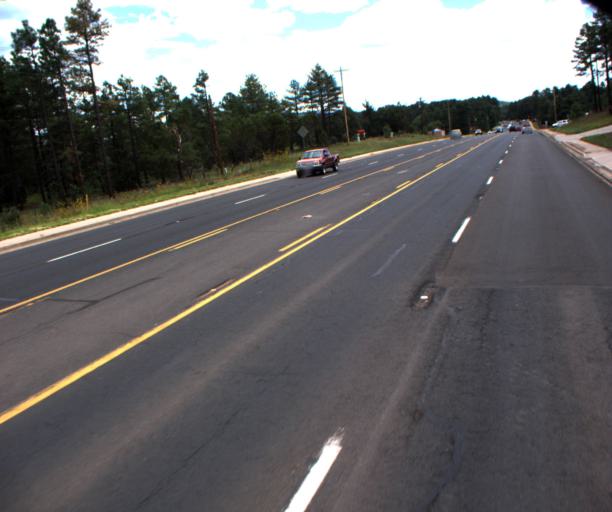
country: US
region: Arizona
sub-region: Navajo County
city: Lake of the Woods
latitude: 34.1614
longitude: -109.9844
